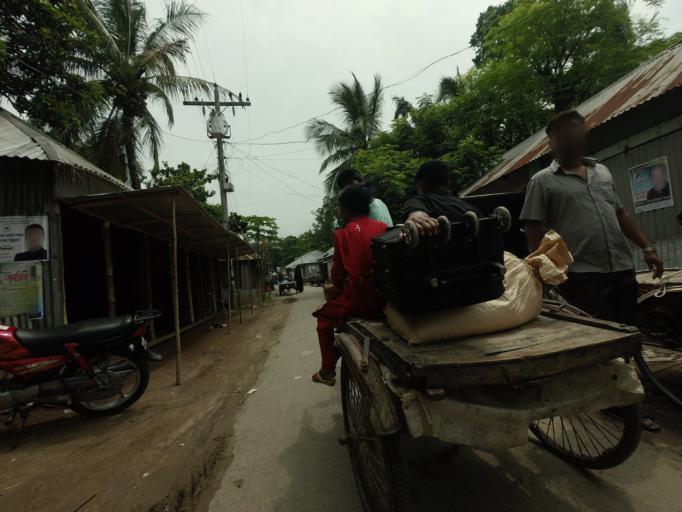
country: BD
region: Khulna
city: Kalia
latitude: 23.0855
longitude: 89.6711
